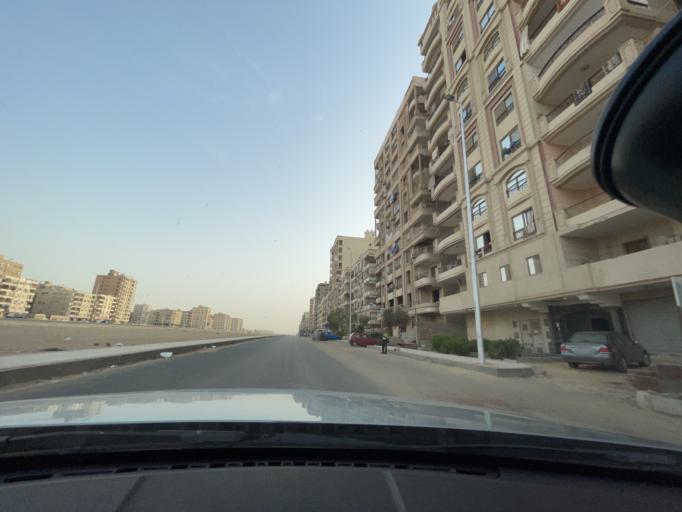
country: EG
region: Muhafazat al Qahirah
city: Cairo
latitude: 30.0546
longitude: 31.3716
